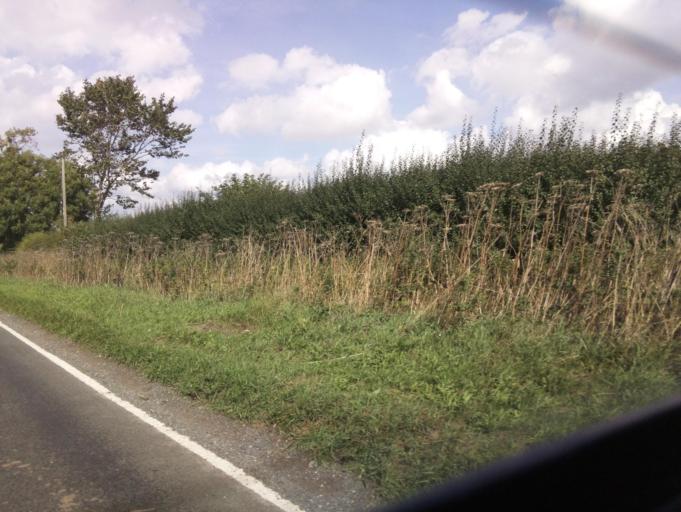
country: GB
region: England
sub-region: Darlington
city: High Coniscliffe
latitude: 54.5076
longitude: -1.6712
